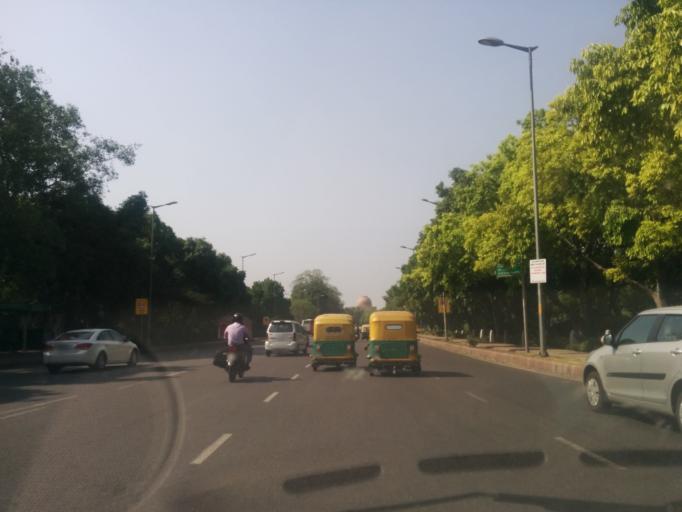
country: IN
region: NCT
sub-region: New Delhi
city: New Delhi
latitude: 28.6139
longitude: 77.2346
